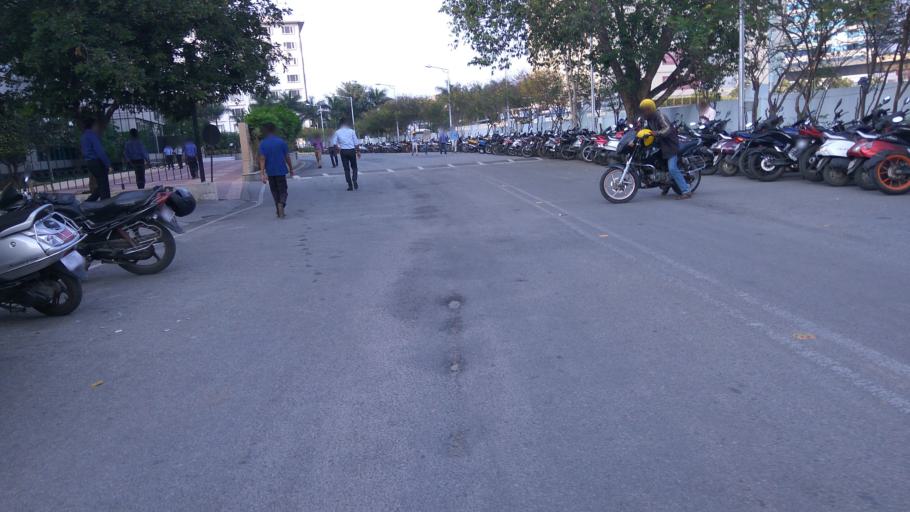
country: IN
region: Karnataka
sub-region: Bangalore Urban
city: Bangalore
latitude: 12.8996
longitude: 77.6314
